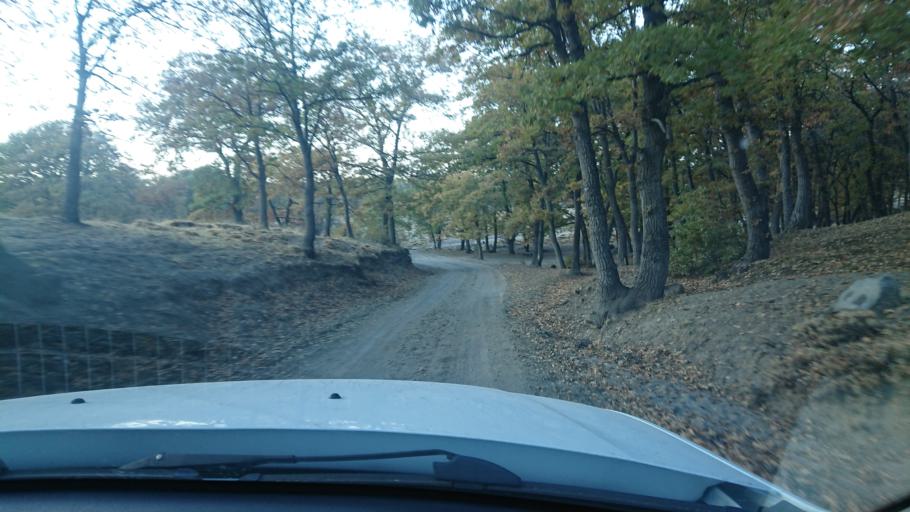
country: TR
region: Aksaray
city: Taspinar
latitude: 38.1658
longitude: 34.2065
